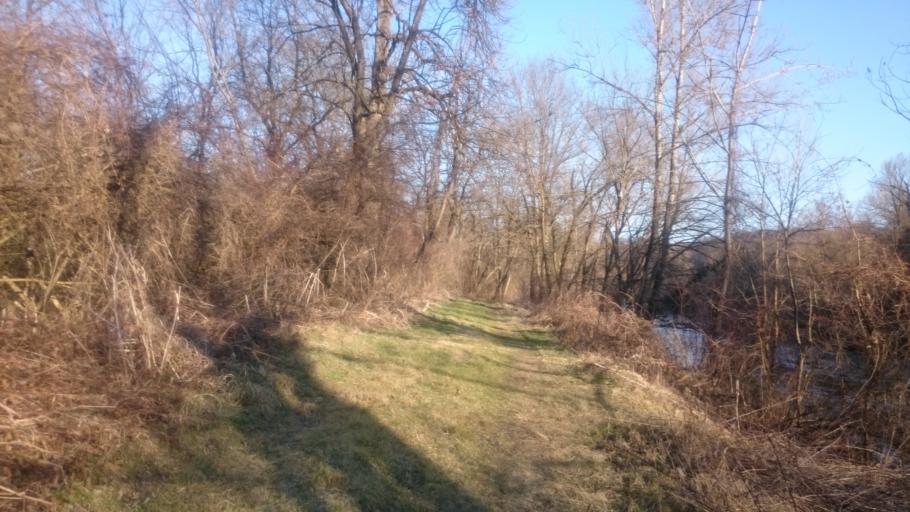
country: SI
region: Sentilj
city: Selnica ob Muri
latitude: 46.6975
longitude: 15.7135
